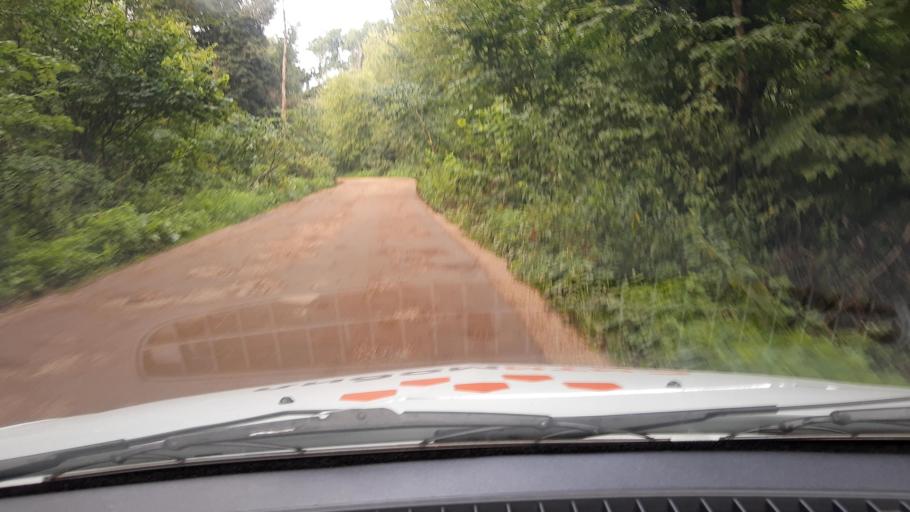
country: RU
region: Bashkortostan
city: Kabakovo
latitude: 54.7066
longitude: 56.1372
